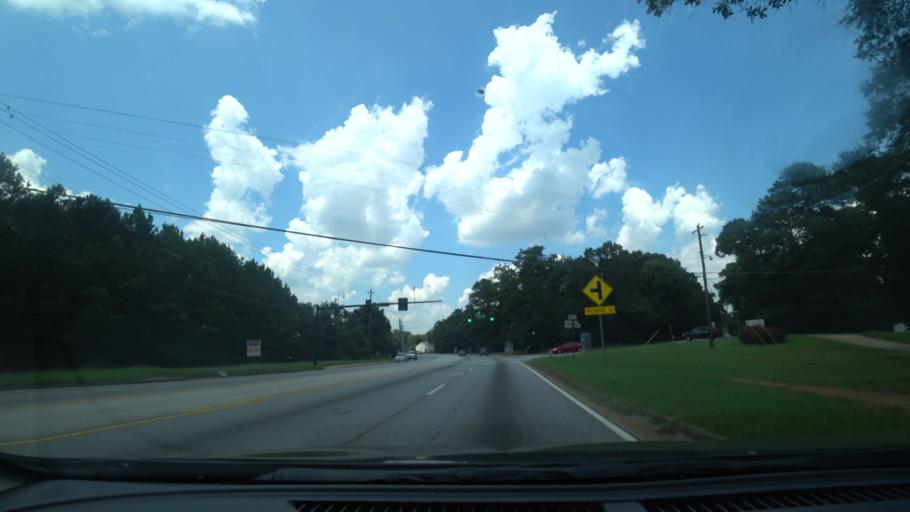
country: US
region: Georgia
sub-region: DeKalb County
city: Belvedere Park
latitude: 33.7435
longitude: -84.2186
